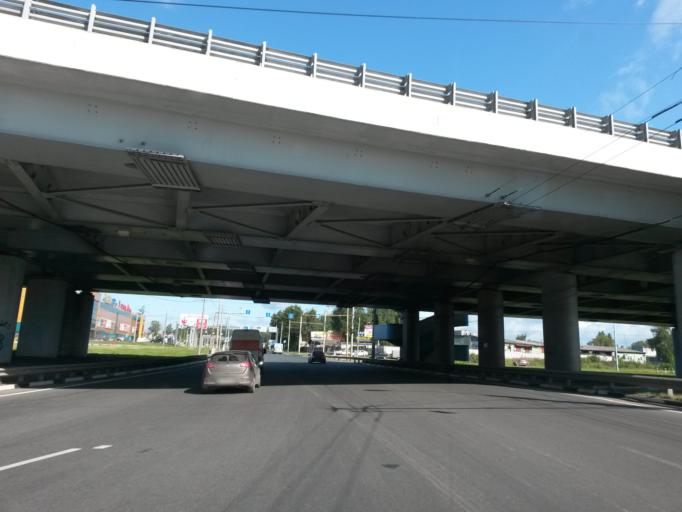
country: RU
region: Jaroslavl
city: Yaroslavl
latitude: 57.6688
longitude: 39.8417
